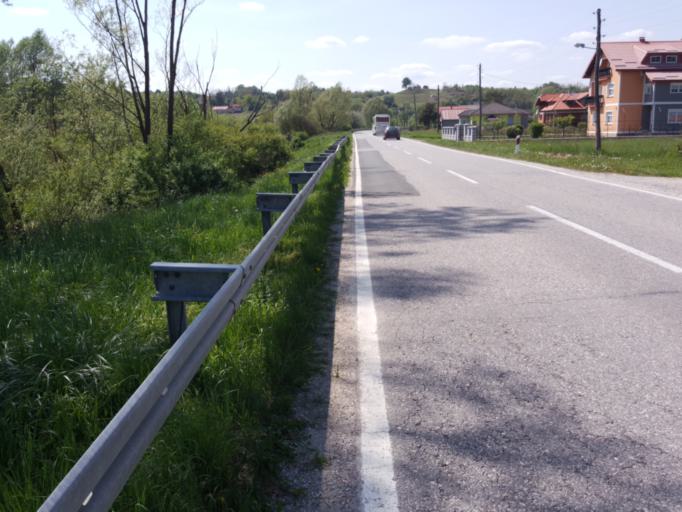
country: HR
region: Varazdinska
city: Lepoglava
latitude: 46.2260
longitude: 15.9741
